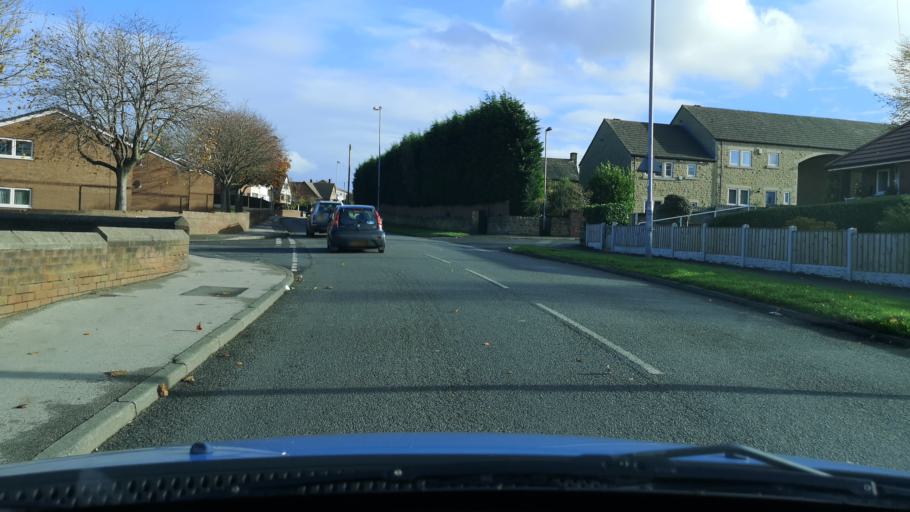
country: GB
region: England
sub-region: City and Borough of Wakefield
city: Crofton
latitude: 53.6541
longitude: -1.4262
